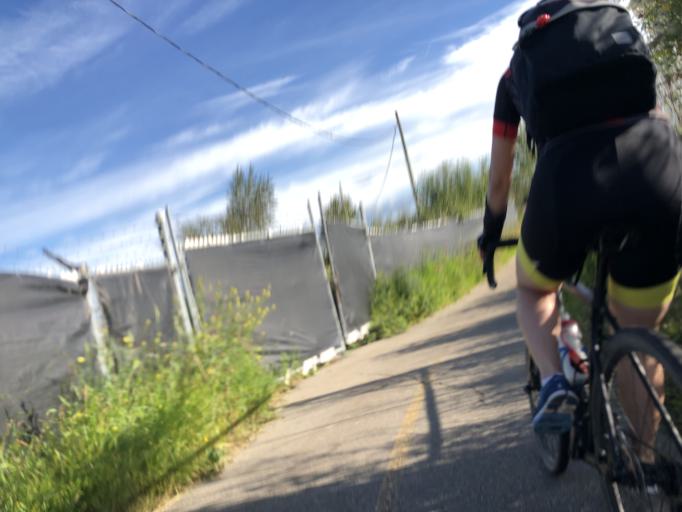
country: CA
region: Alberta
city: Calgary
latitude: 50.9587
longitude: -114.0246
